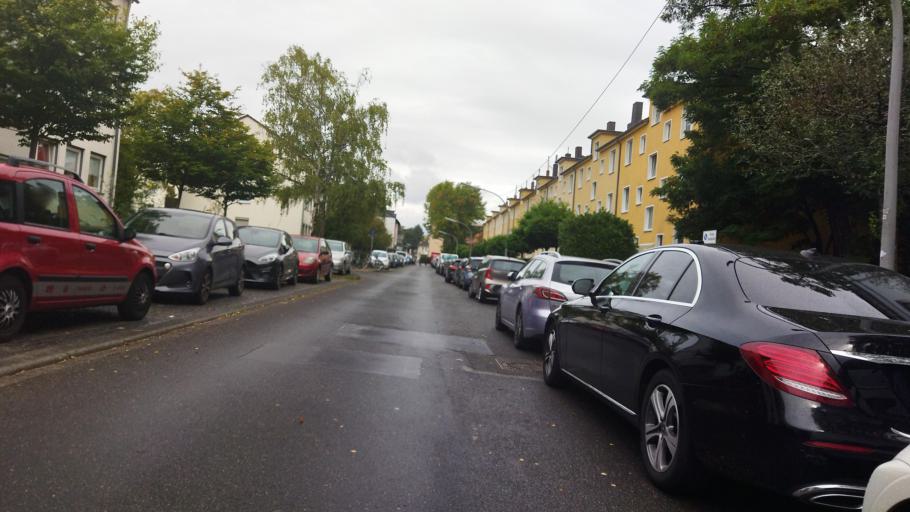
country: DE
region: North Rhine-Westphalia
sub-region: Regierungsbezirk Koln
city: Riehl
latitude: 50.9724
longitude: 6.9653
